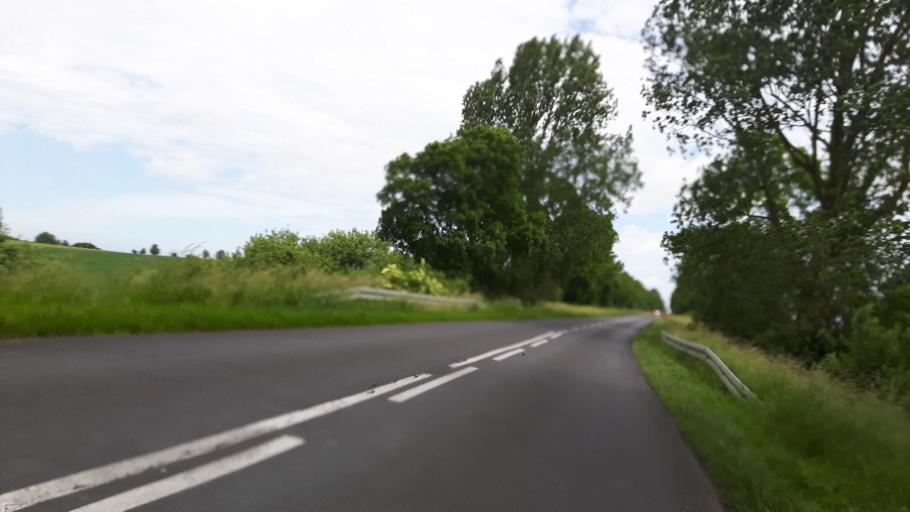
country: PL
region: West Pomeranian Voivodeship
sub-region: Powiat gryficki
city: Trzebiatow
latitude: 54.0302
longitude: 15.2412
